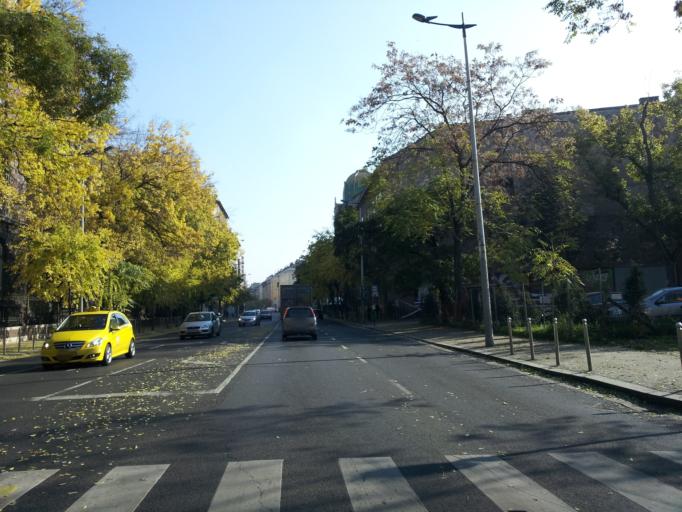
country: HU
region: Budapest
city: Budapest VIII. keruelet
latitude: 47.4872
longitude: 19.0669
